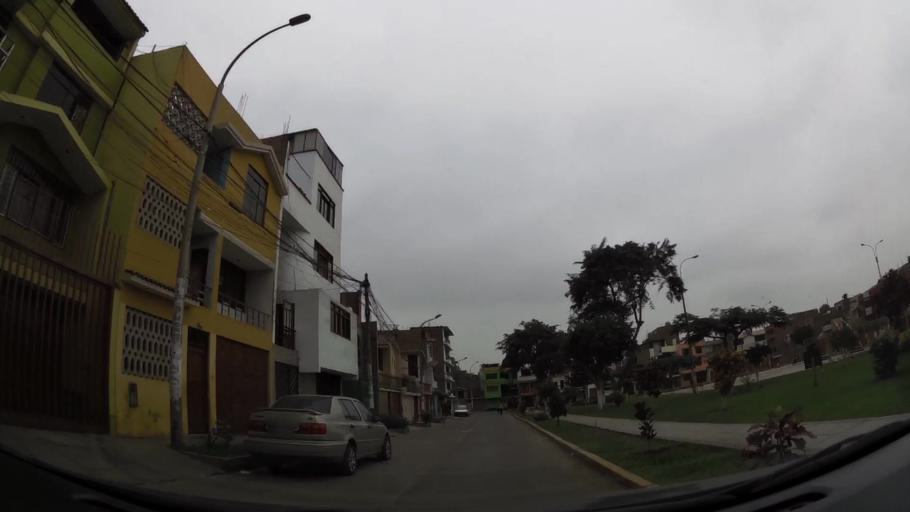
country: PE
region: Lima
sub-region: Lima
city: Independencia
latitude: -11.9599
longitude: -77.0597
